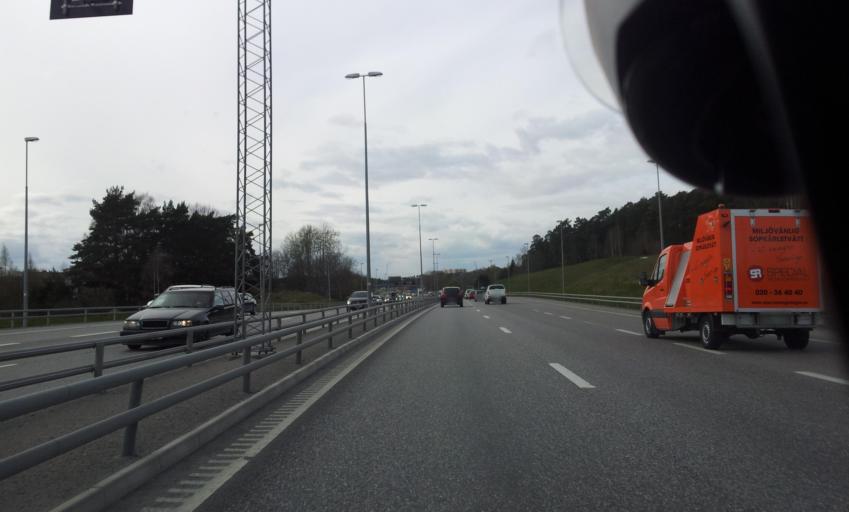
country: SE
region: Stockholm
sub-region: Jarfalla Kommun
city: Jakobsberg
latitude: 59.4016
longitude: 17.8771
